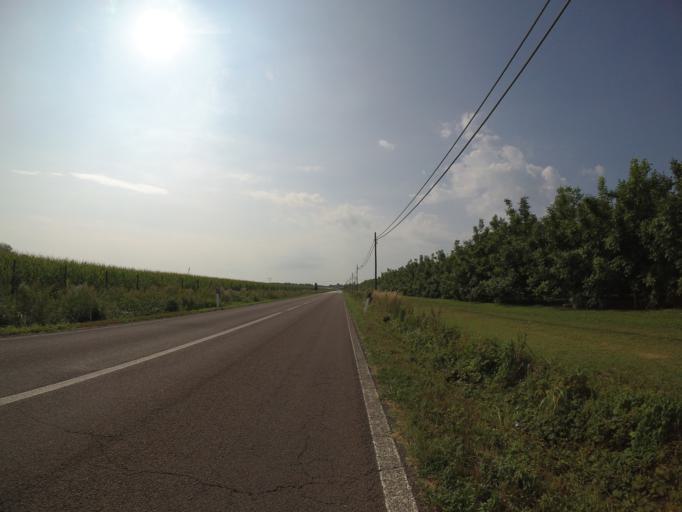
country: IT
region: Friuli Venezia Giulia
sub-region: Provincia di Udine
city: Pocenia
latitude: 45.8348
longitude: 13.0779
